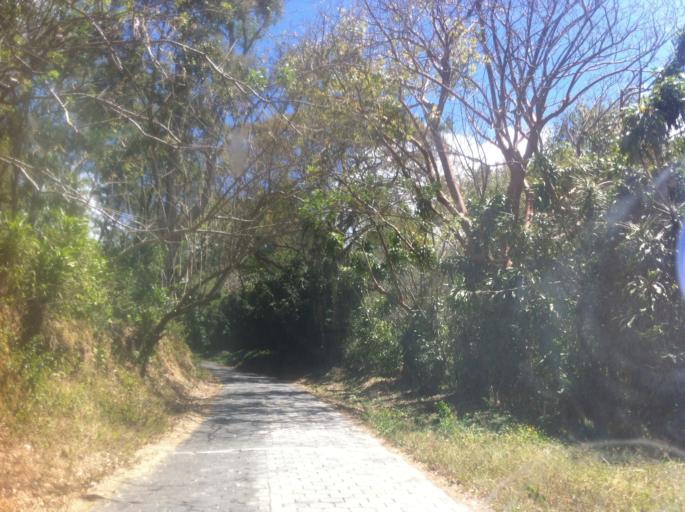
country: NI
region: Granada
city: Diriomo
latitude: 11.8395
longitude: -85.9978
